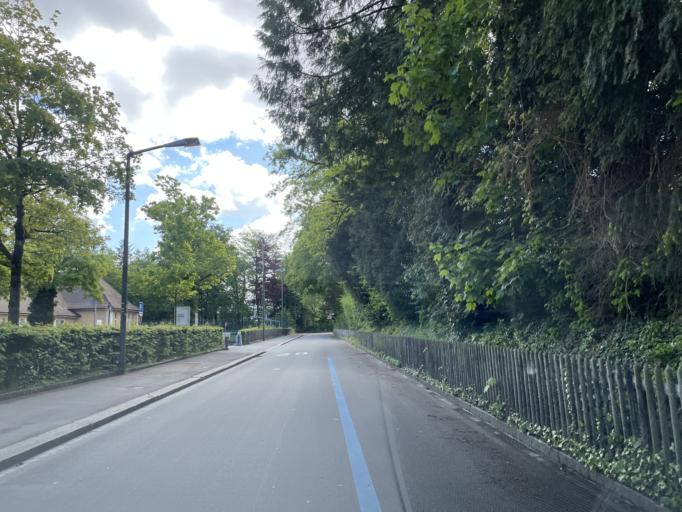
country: CH
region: Zurich
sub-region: Bezirk Winterthur
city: Stadt Winterthur (Kreis 1) / Heiligberg
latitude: 47.4955
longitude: 8.7251
